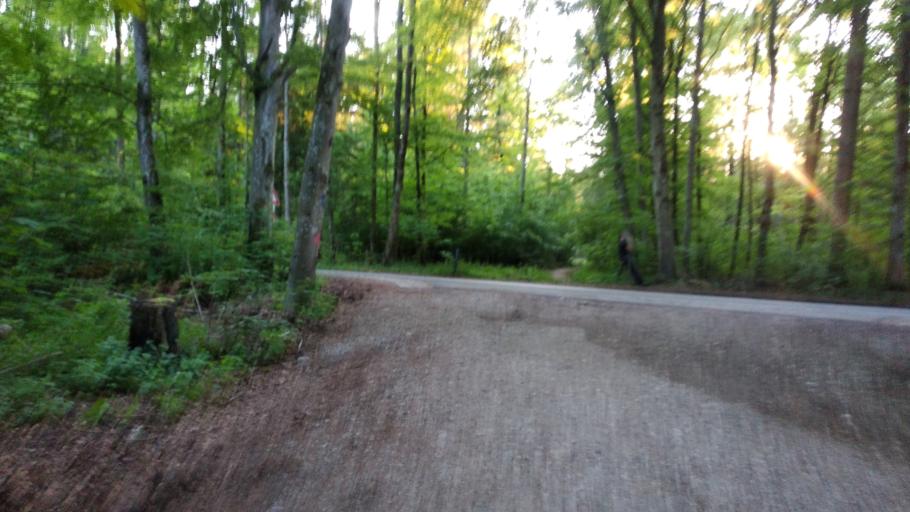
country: DE
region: Bavaria
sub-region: Upper Bavaria
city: Vaterstetten
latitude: 48.0880
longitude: 11.7824
